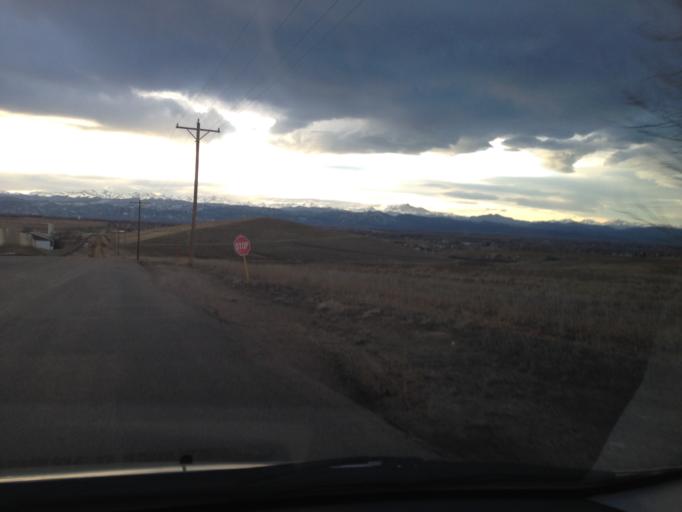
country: US
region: Colorado
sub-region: Boulder County
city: Erie
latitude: 40.0293
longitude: -105.0226
